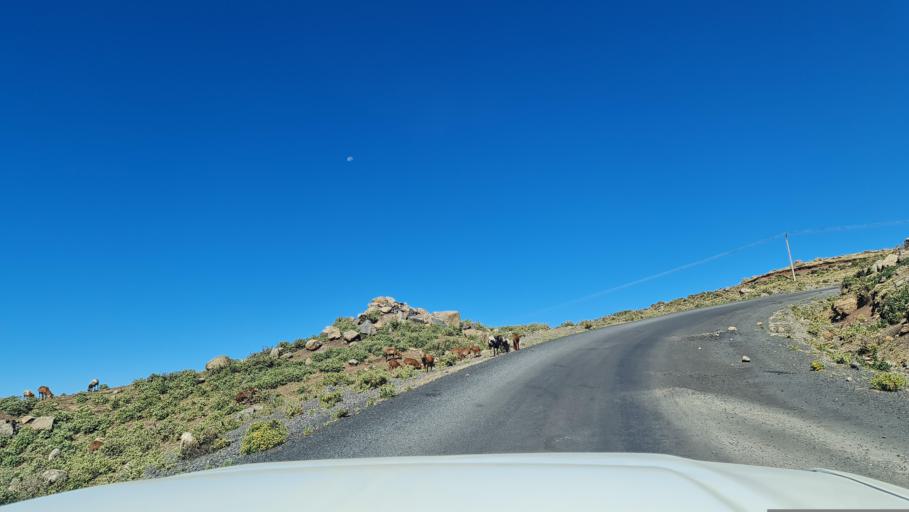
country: ET
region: Amhara
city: Debark'
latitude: 13.1388
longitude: 38.1773
